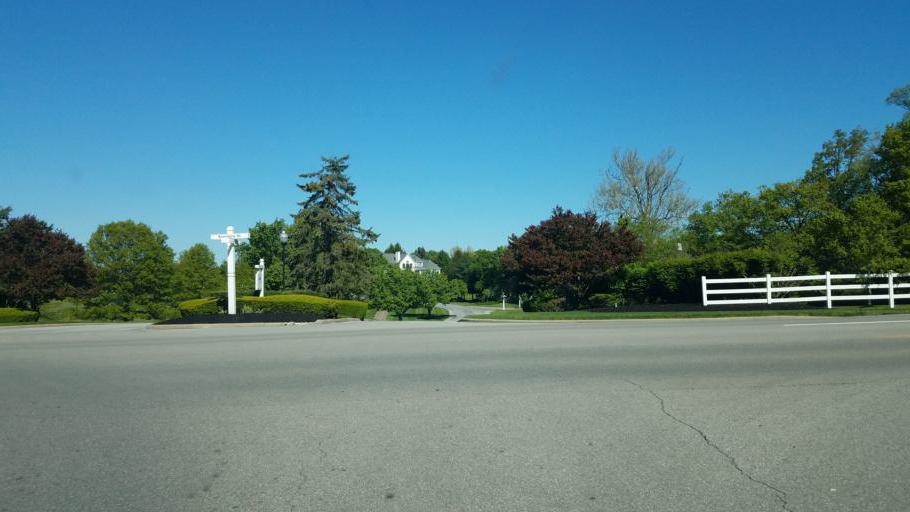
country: US
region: Ohio
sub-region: Franklin County
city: Westerville
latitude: 40.1647
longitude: -82.9402
